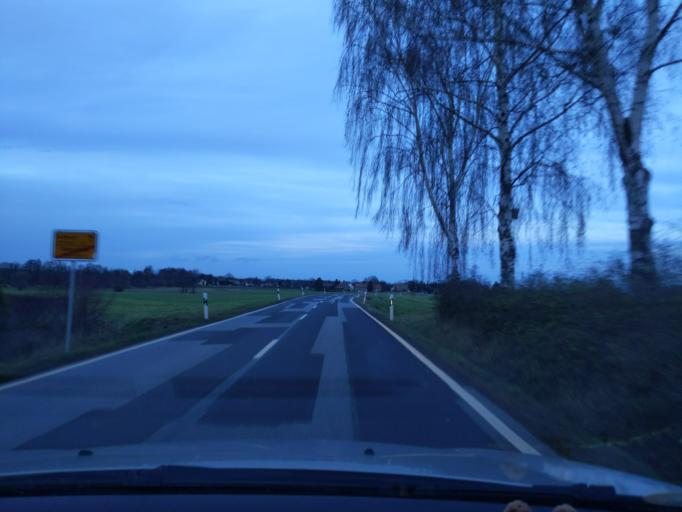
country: DE
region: Saxony
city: Malschwitz
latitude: 51.2202
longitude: 14.4988
